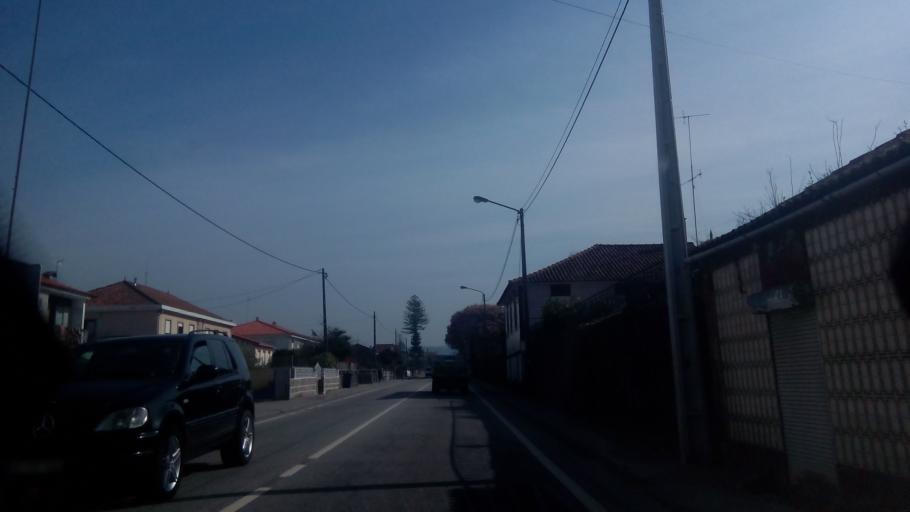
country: PT
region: Viana do Castelo
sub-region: Viana do Castelo
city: Meadela
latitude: 41.6832
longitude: -8.7923
